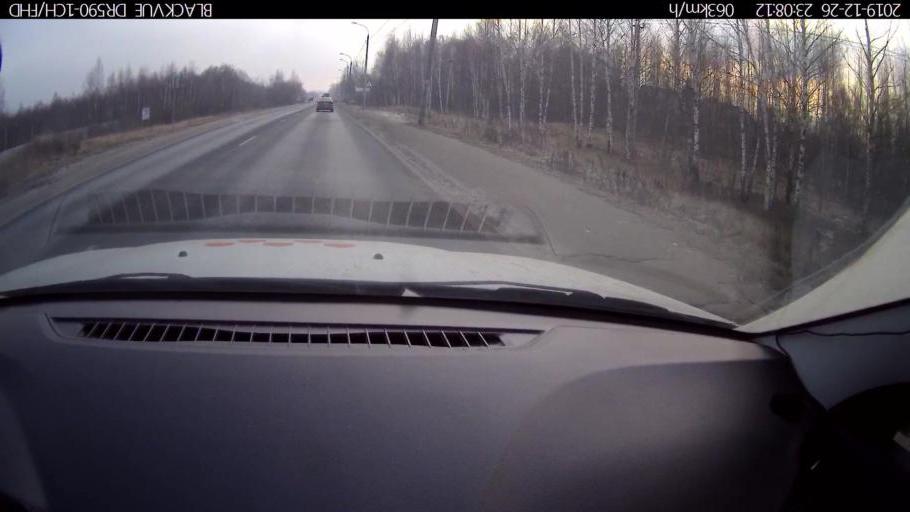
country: RU
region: Nizjnij Novgorod
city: Gorbatovka
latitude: 56.2158
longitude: 43.7587
